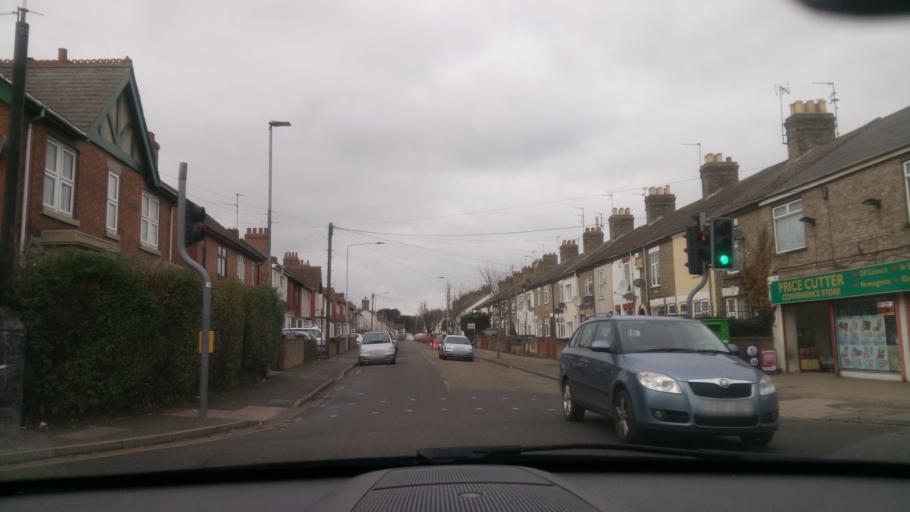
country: GB
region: England
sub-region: Peterborough
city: Peterborough
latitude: 52.5785
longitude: -0.2280
